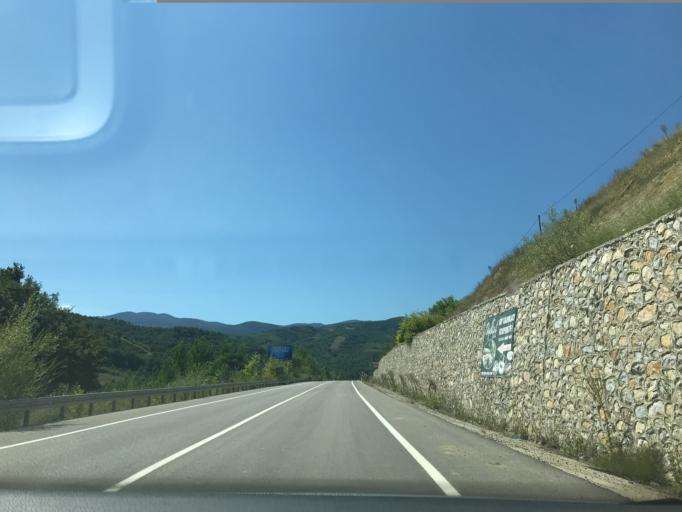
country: TR
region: Bursa
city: Tahtakopru
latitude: 39.9688
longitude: 29.6047
